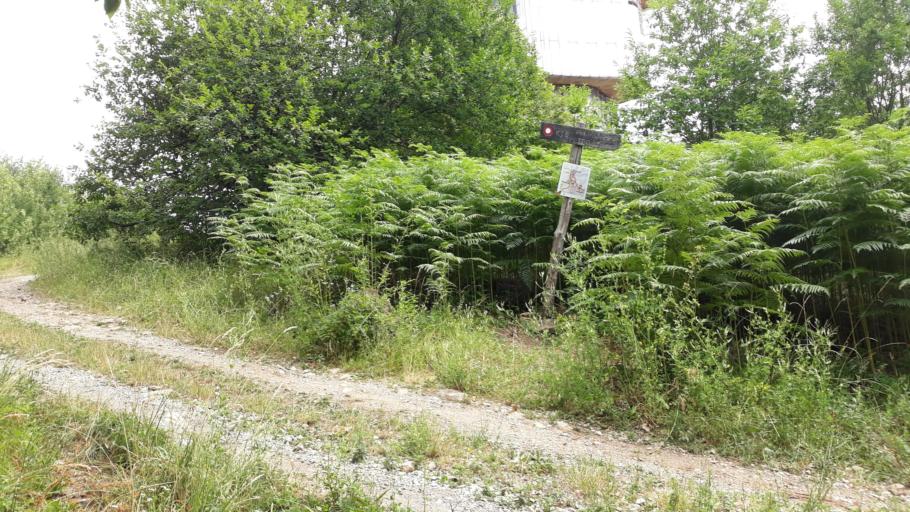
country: HR
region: Sisacko-Moslavacka
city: Gvozd
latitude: 45.3178
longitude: 15.8055
